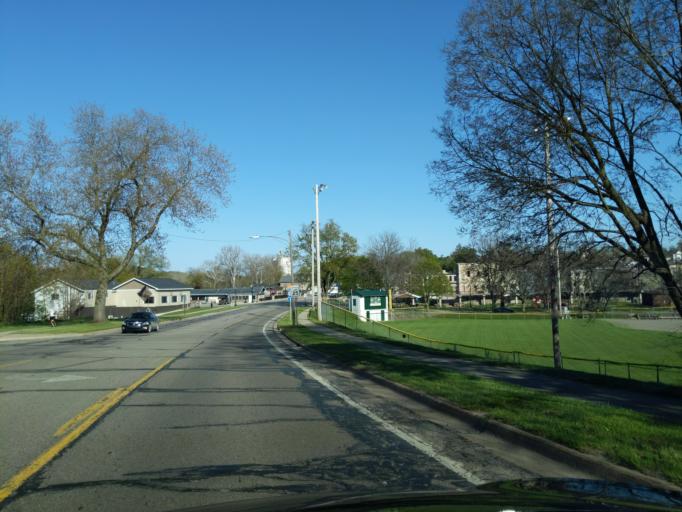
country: US
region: Michigan
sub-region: Ionia County
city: Portland
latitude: 42.8715
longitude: -84.9054
